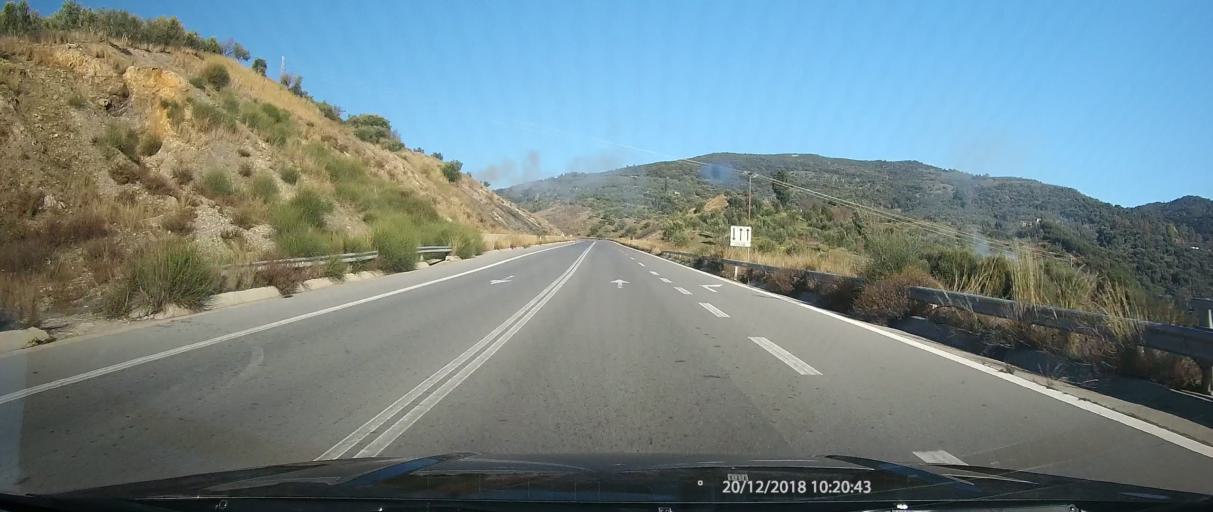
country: GR
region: Peloponnese
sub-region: Nomos Lakonias
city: Magoula
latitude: 37.1511
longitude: 22.4340
